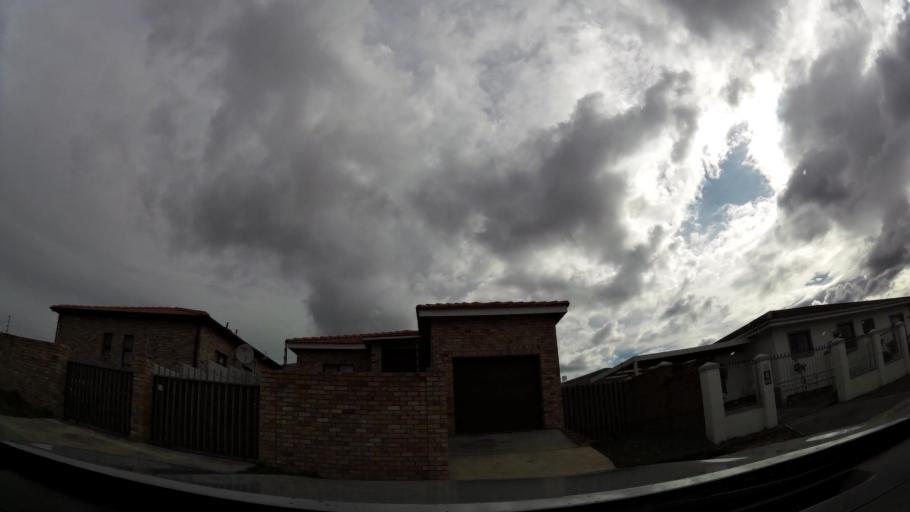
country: ZA
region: Eastern Cape
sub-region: Nelson Mandela Bay Metropolitan Municipality
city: Port Elizabeth
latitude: -33.9300
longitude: 25.5085
